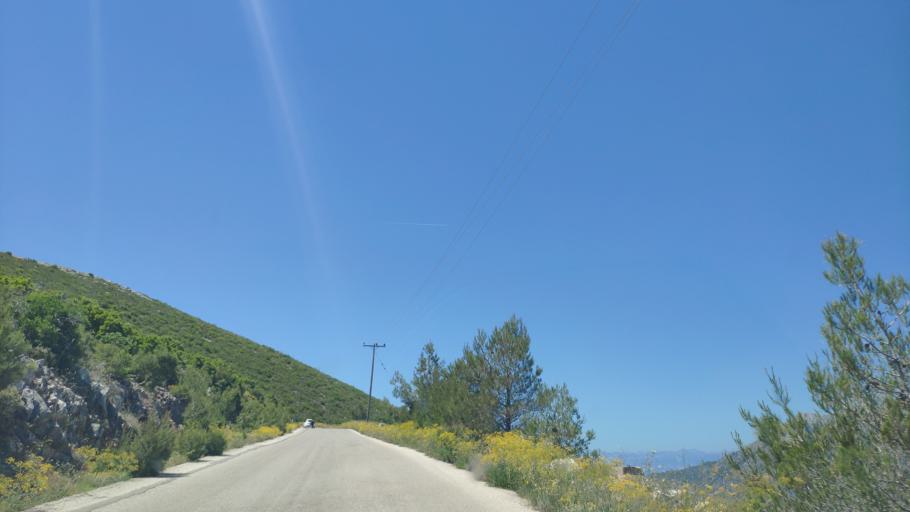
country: GR
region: Central Greece
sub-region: Nomos Voiotias
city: Kaparellion
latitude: 38.2011
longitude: 23.1542
